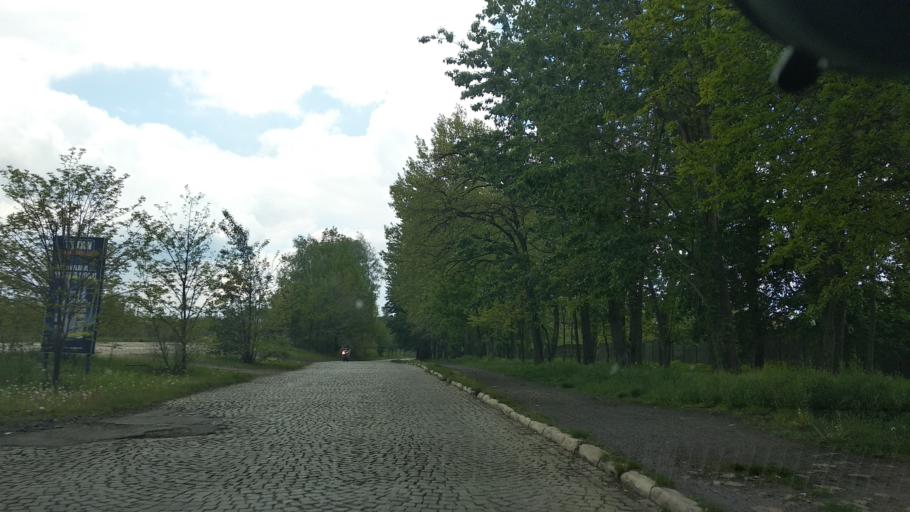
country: PL
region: Silesian Voivodeship
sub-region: Katowice
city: Katowice
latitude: 50.2643
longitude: 18.9916
